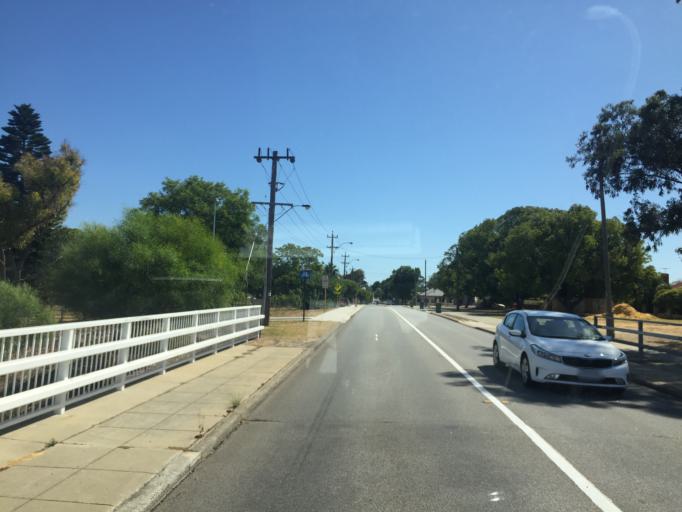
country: AU
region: Western Australia
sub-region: Belmont
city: Redcliffe
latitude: -31.9374
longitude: 115.9449
